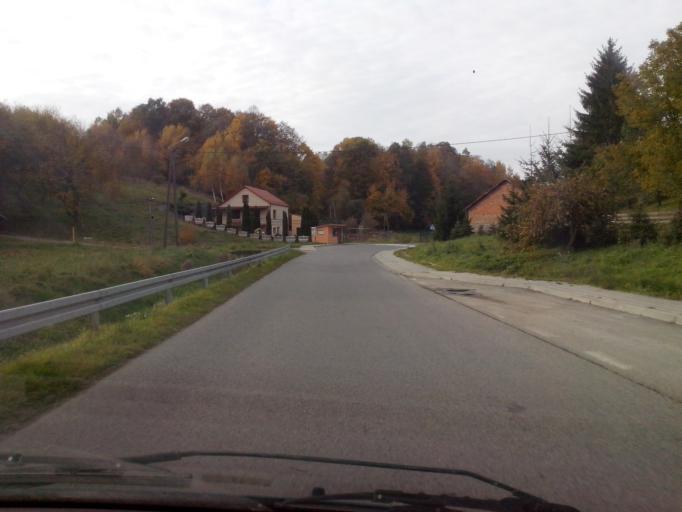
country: PL
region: Subcarpathian Voivodeship
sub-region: Powiat strzyzowski
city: Wisniowa
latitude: 49.8825
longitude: 21.6708
